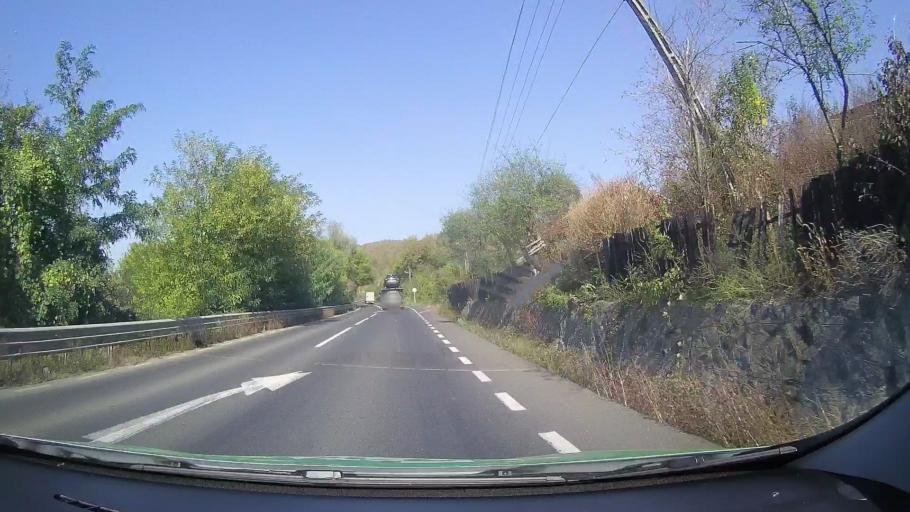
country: RO
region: Arad
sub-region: Comuna Bata
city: Bata
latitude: 46.0422
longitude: 22.0595
